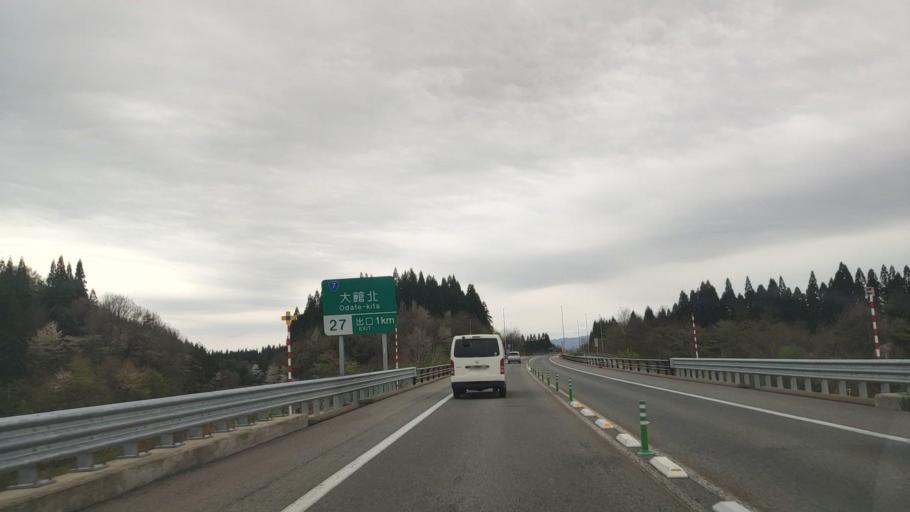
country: JP
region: Akita
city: Odate
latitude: 40.3114
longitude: 140.5776
